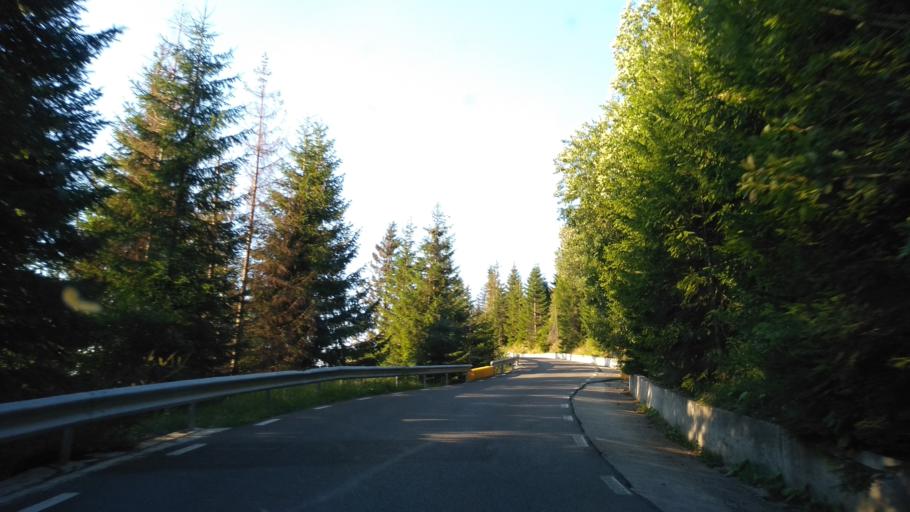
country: RO
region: Prahova
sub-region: Oras Sinaia
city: Sinaia
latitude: 45.3214
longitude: 25.4836
